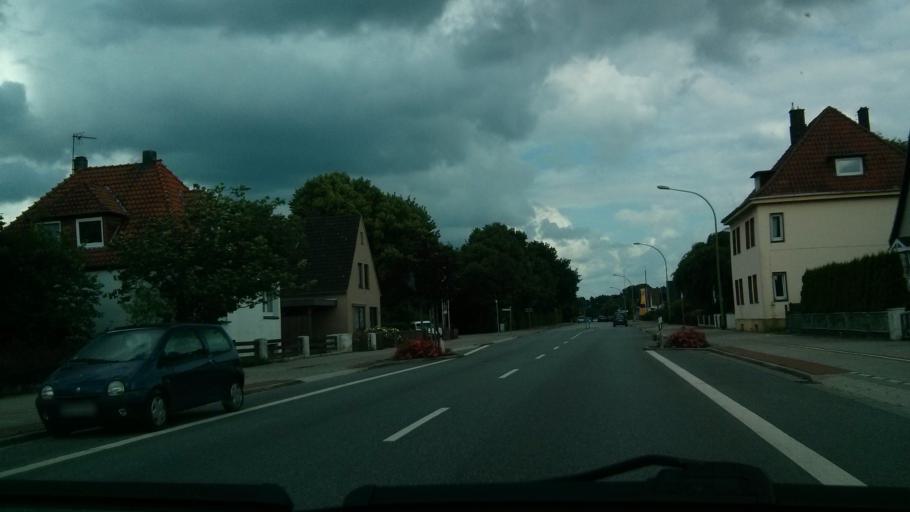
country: DE
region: Bremen
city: Bremerhaven
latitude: 53.5301
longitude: 8.6088
